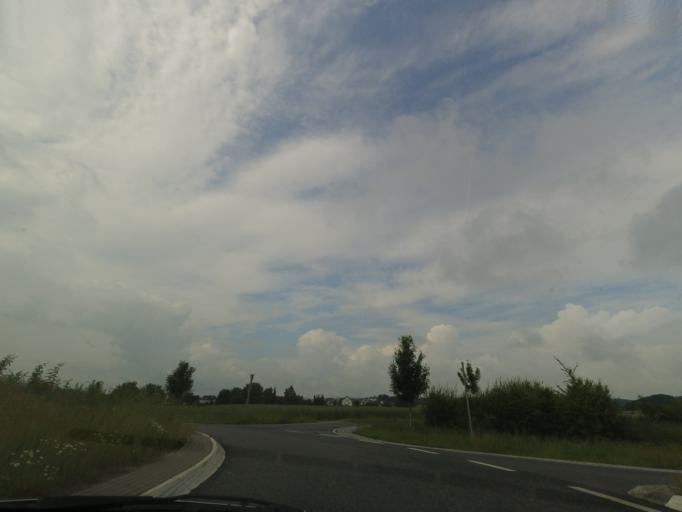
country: DE
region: Hesse
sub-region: Regierungsbezirk Giessen
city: Fronhausen
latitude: 50.7506
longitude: 8.7212
